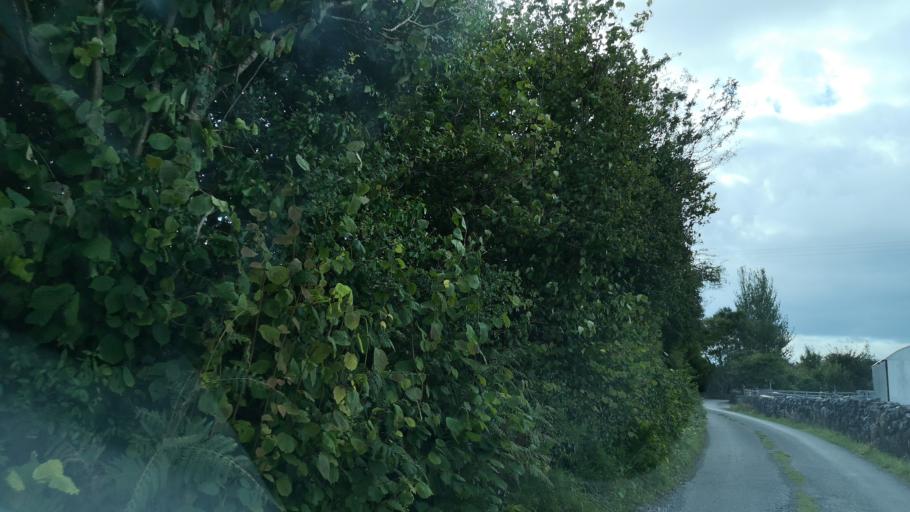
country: IE
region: Connaught
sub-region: County Galway
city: Moycullen
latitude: 53.3605
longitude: -9.1706
